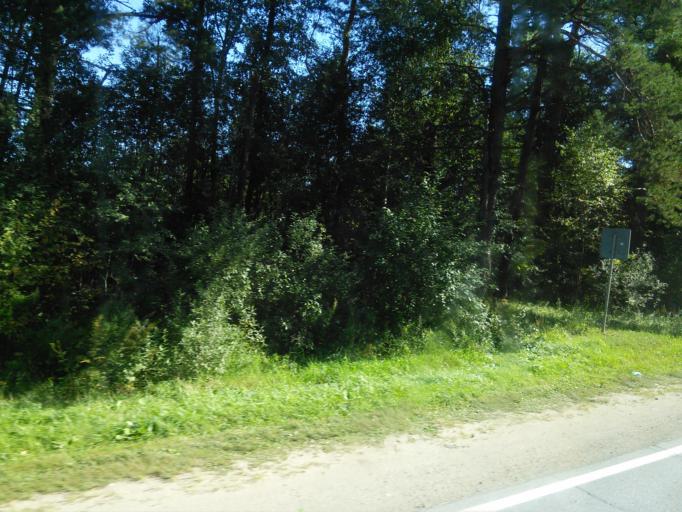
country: RU
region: Jaroslavl
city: Uglich
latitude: 57.4867
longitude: 38.3583
